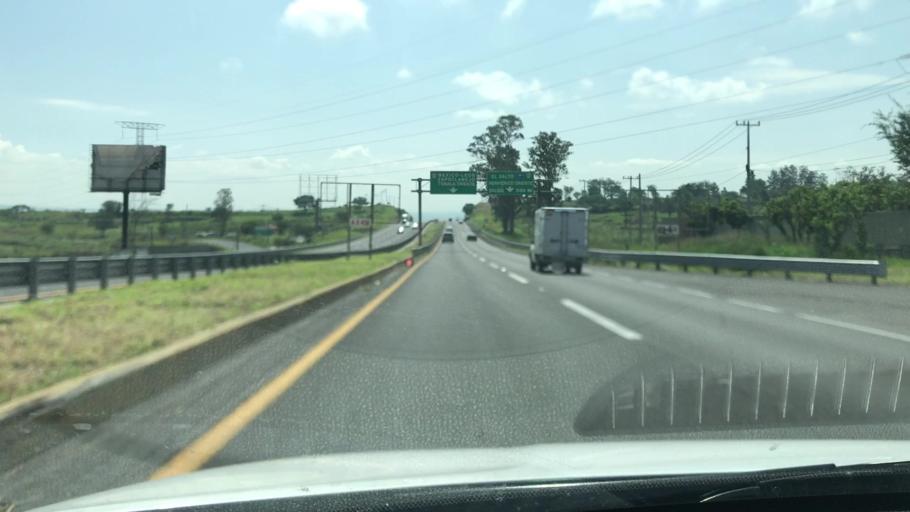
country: MX
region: Jalisco
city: Tonala
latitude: 20.6167
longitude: -103.2260
